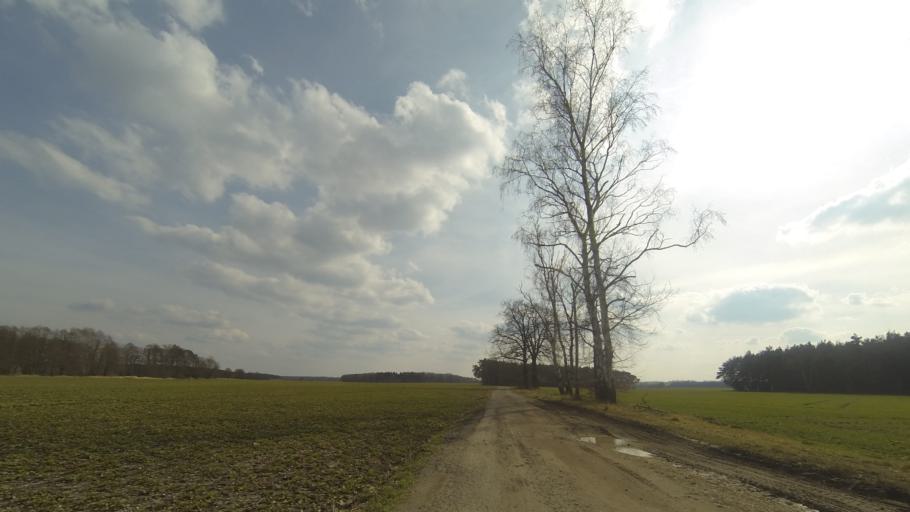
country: DE
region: Saxony
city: Schonfeld
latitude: 51.2567
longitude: 13.7013
